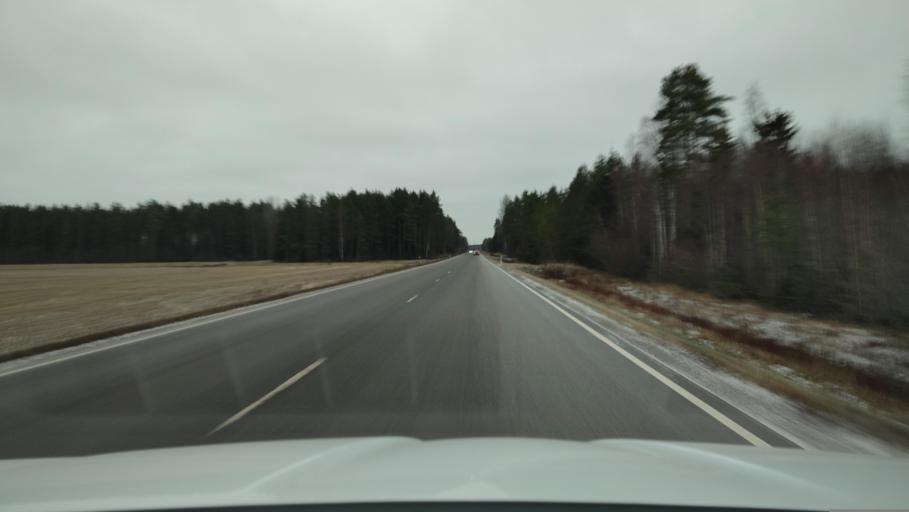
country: FI
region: Ostrobothnia
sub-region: Sydosterbotten
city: Naerpes
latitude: 62.5291
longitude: 21.4616
